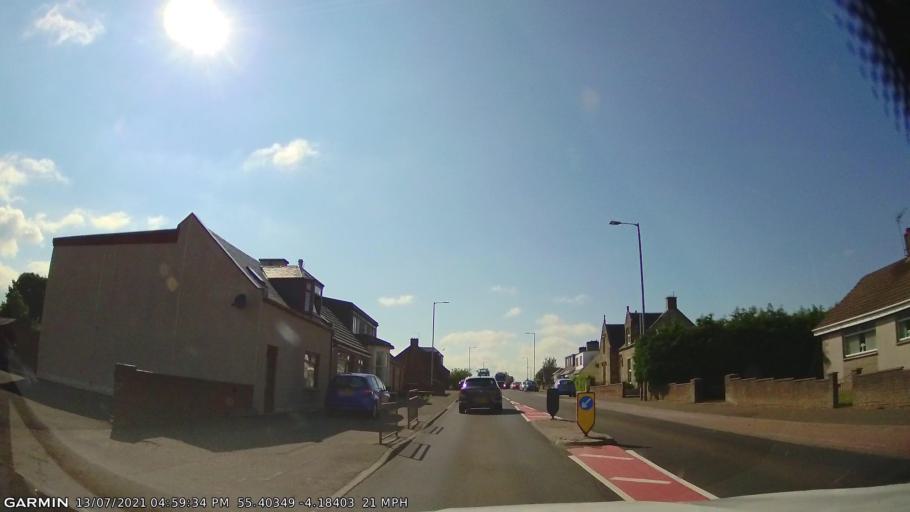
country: GB
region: Scotland
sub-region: East Ayrshire
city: New Cumnock
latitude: 55.4035
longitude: -4.1842
